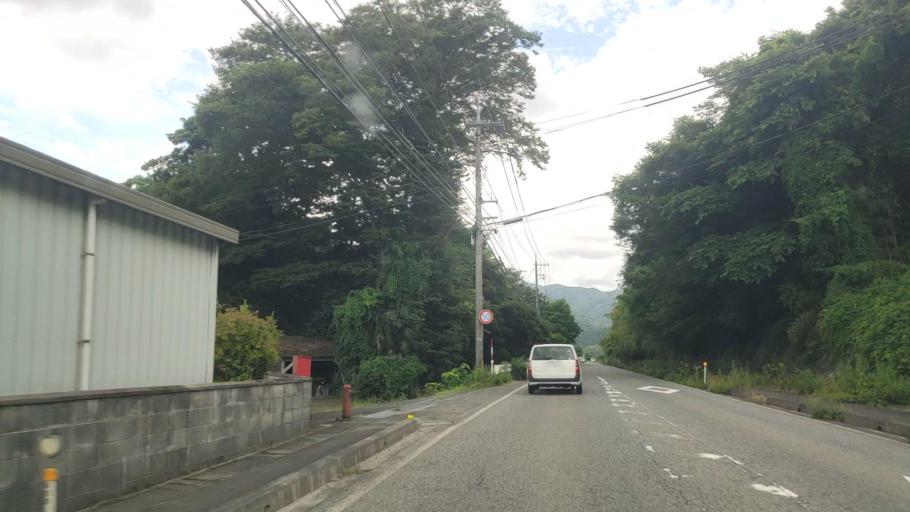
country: JP
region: Tottori
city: Yonago
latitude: 35.3399
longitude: 133.4340
